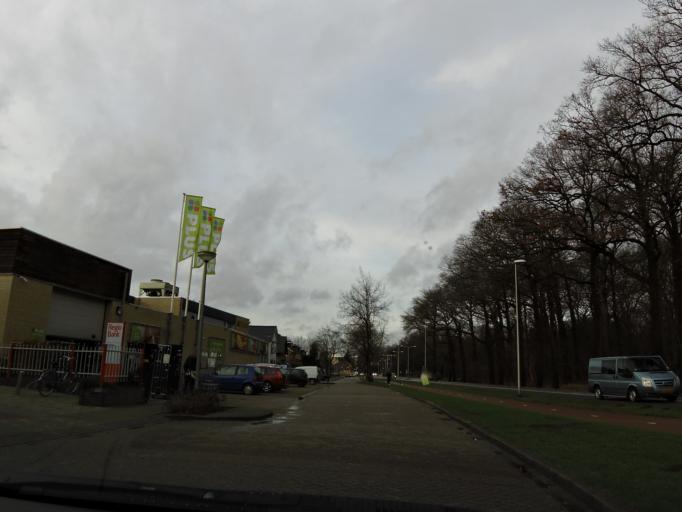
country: NL
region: Limburg
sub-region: Gemeente Roerdalen
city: Sint Odilienberg
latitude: 51.1433
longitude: 6.0065
